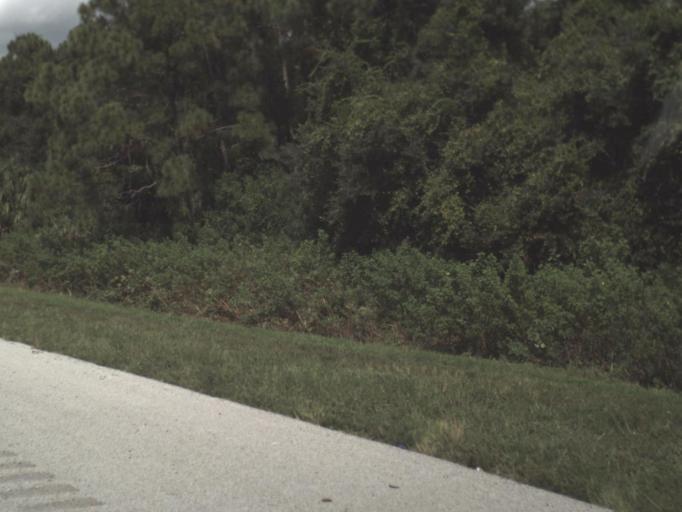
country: US
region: Florida
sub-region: Hillsborough County
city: Ruskin
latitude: 27.6974
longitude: -82.4048
